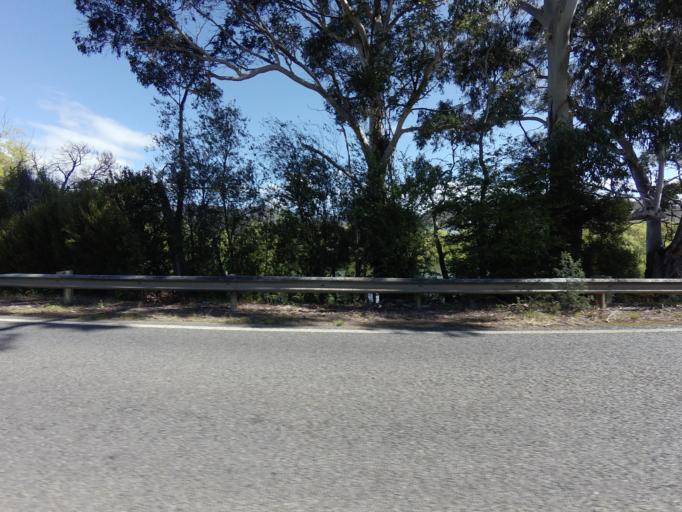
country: AU
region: Tasmania
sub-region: Derwent Valley
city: New Norfolk
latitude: -42.7672
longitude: 147.0247
